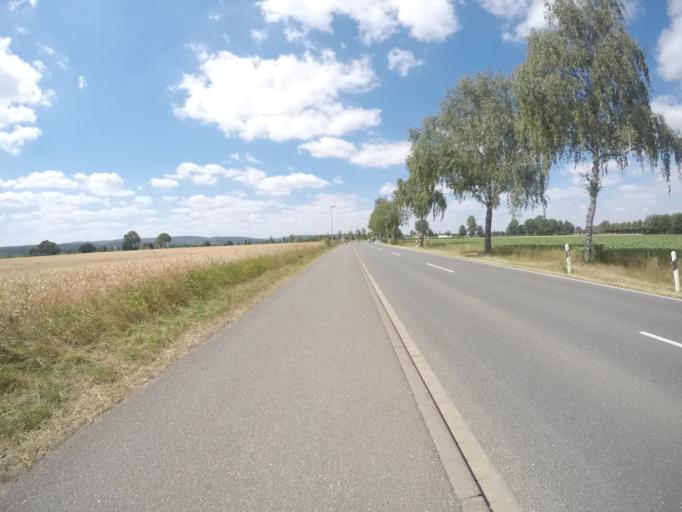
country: DE
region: Lower Saxony
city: Rinteln
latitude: 52.1872
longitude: 9.0653
